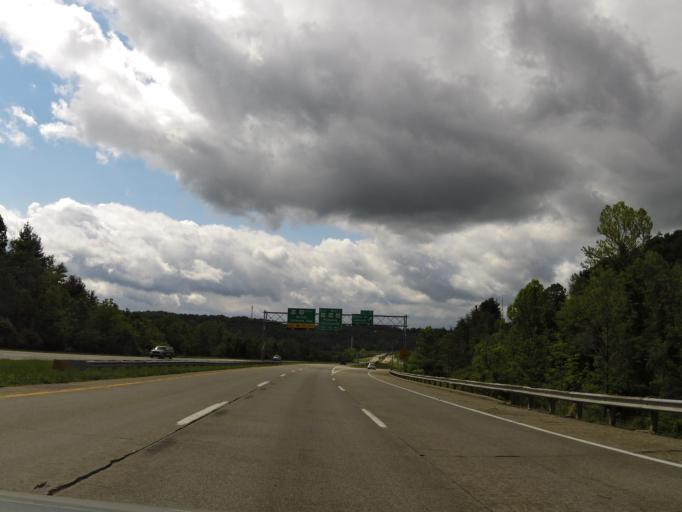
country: US
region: Ohio
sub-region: Athens County
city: Athens
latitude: 39.3433
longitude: -82.0812
